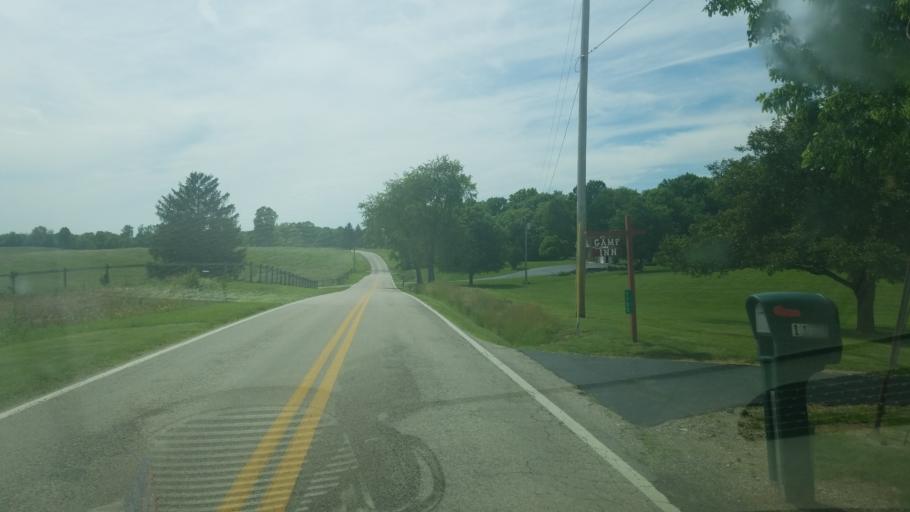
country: US
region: Ohio
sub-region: Delaware County
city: Delaware
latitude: 40.3356
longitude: -83.0457
